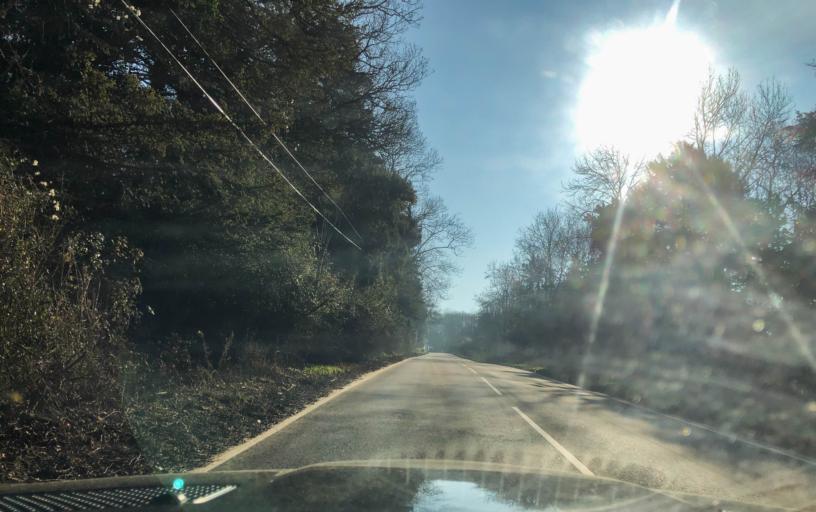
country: GB
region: England
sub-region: Warwickshire
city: Wellesbourne Mountford
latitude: 52.1800
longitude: -1.5714
